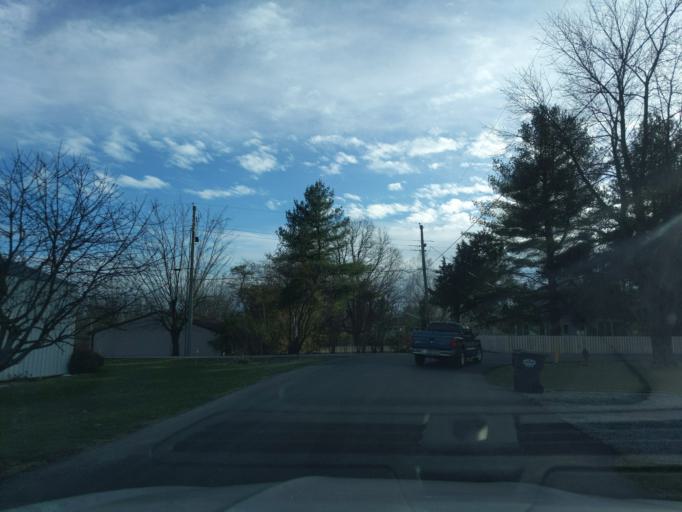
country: US
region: Indiana
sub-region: Decatur County
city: Westport
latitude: 39.1781
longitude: -85.5688
